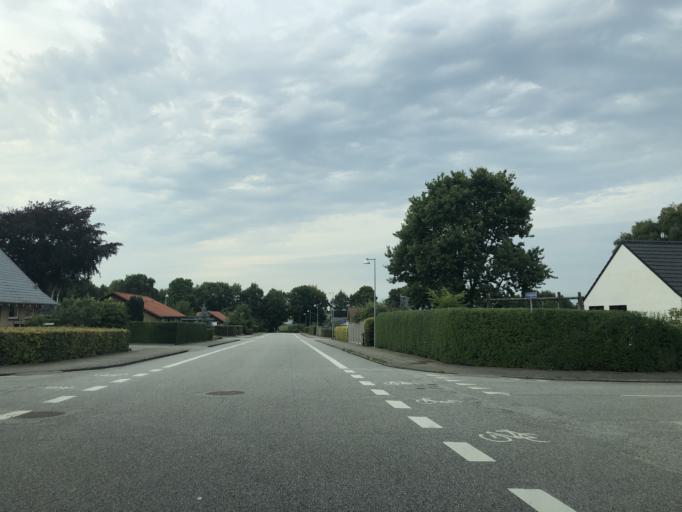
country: DK
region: Central Jutland
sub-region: Herning Kommune
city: Herning
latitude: 56.1468
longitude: 8.9511
